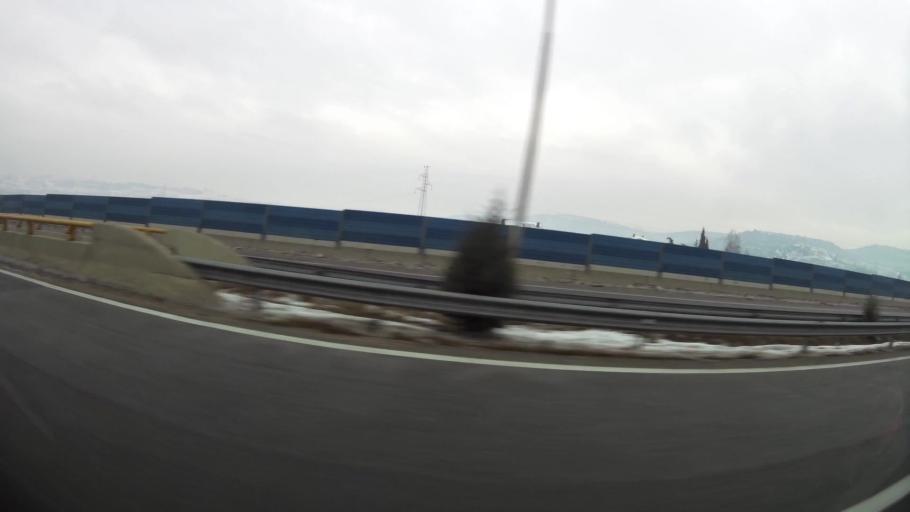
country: MK
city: Kondovo
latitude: 42.0324
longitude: 21.3317
